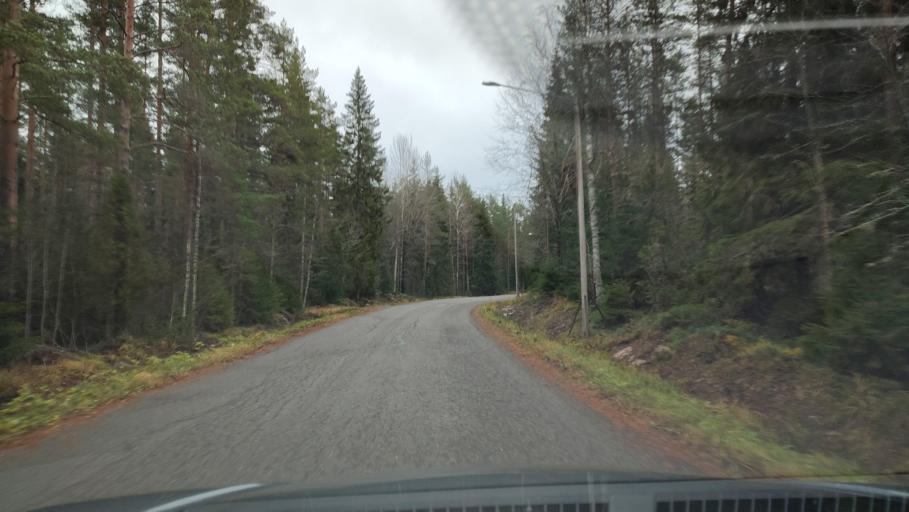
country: FI
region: Southern Ostrobothnia
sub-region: Suupohja
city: Karijoki
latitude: 62.1348
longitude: 21.5745
